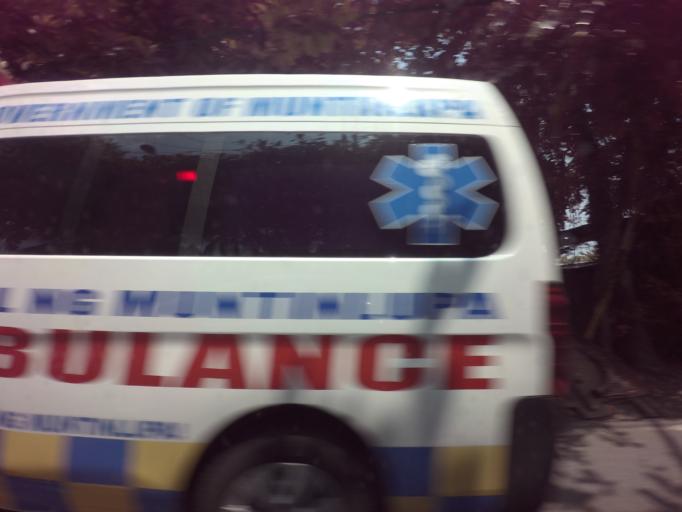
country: PH
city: Sambayanihan People's Village
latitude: 14.4453
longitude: 121.0505
